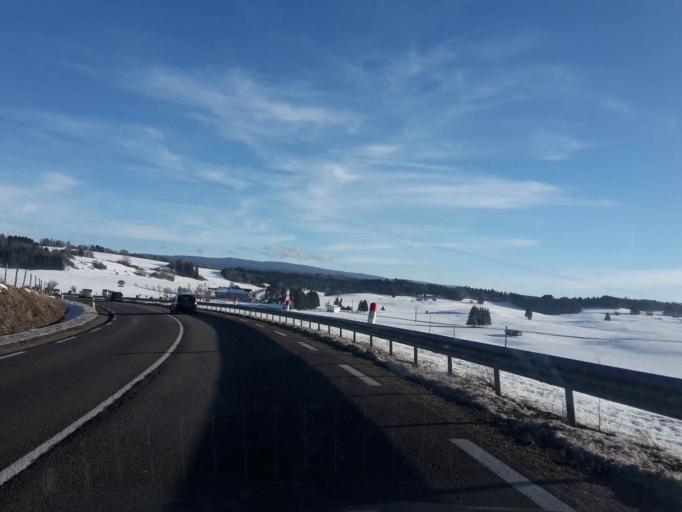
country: FR
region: Franche-Comte
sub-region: Departement du Doubs
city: Doubs
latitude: 46.9834
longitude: 6.3318
